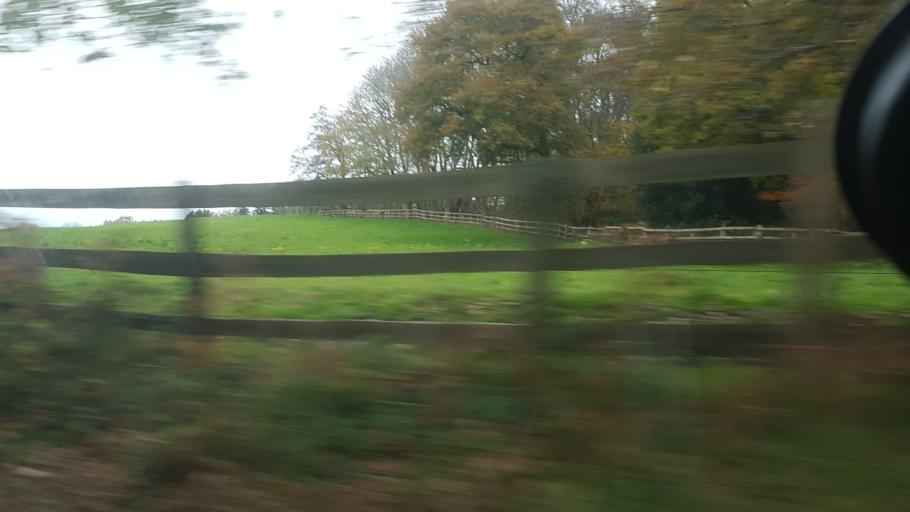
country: GB
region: England
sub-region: Hampshire
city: Yateley
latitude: 51.3569
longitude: -0.8249
